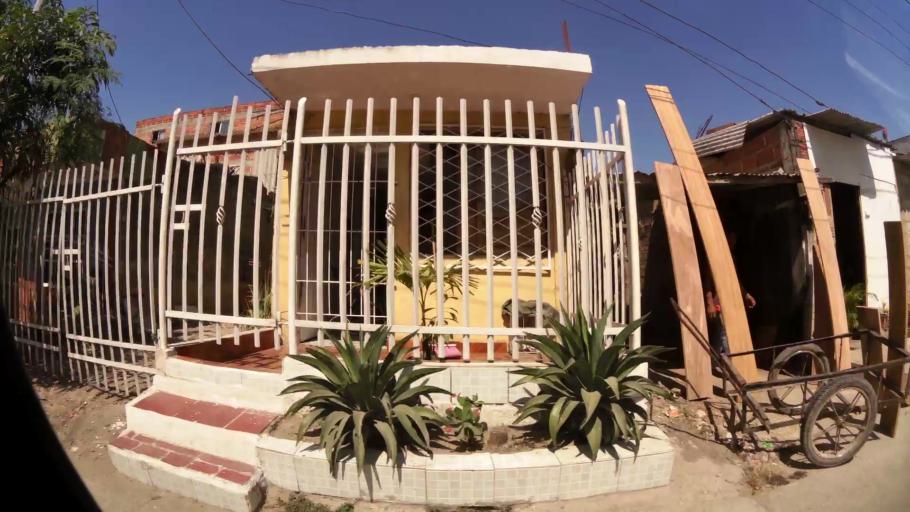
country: CO
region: Bolivar
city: Cartagena
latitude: 10.3898
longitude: -75.4537
